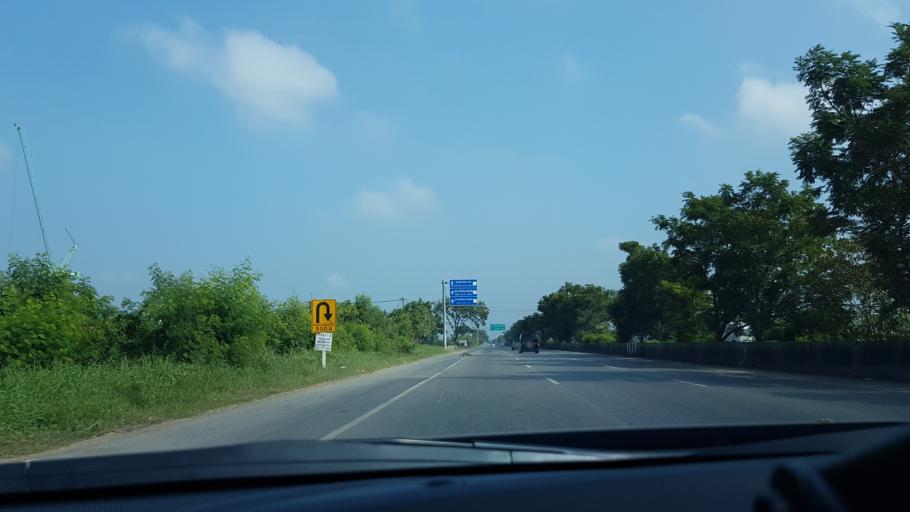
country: TH
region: Pathum Thani
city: Sam Khok
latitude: 14.1349
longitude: 100.5693
